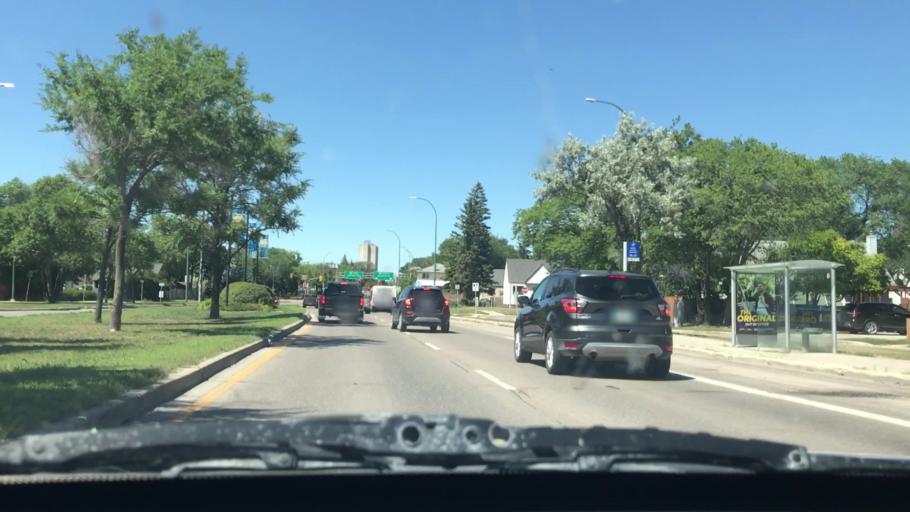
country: CA
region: Manitoba
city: Winnipeg
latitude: 49.8579
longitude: -97.1283
